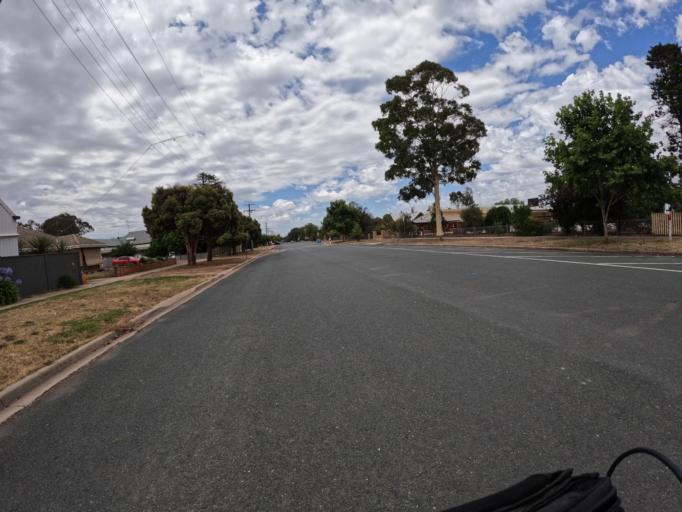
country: AU
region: Victoria
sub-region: Greater Shepparton
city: Shepparton
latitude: -36.6165
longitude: 145.2154
